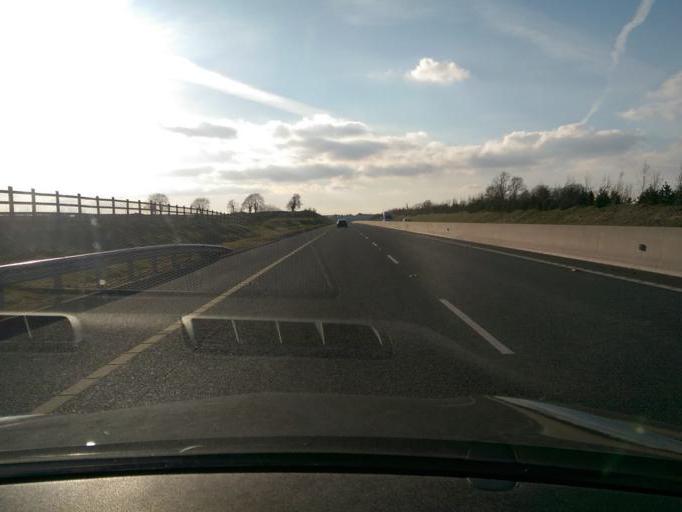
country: IE
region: Leinster
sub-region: Laois
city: Rathdowney
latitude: 52.9192
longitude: -7.5596
